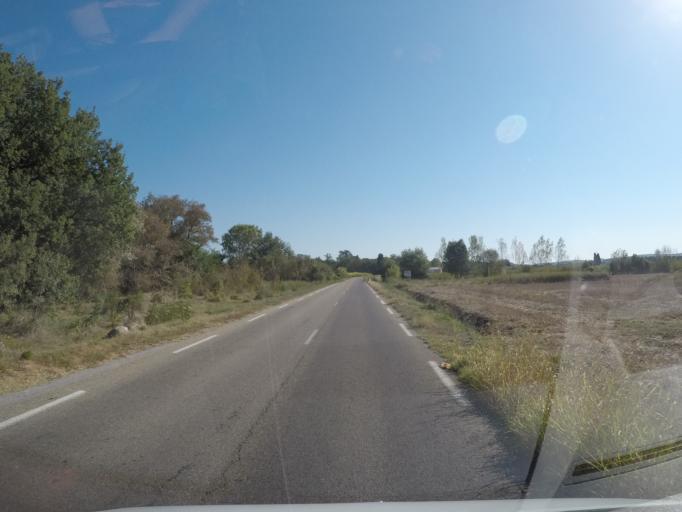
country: FR
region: Languedoc-Roussillon
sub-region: Departement du Gard
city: Lezan
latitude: 44.0243
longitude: 4.0670
